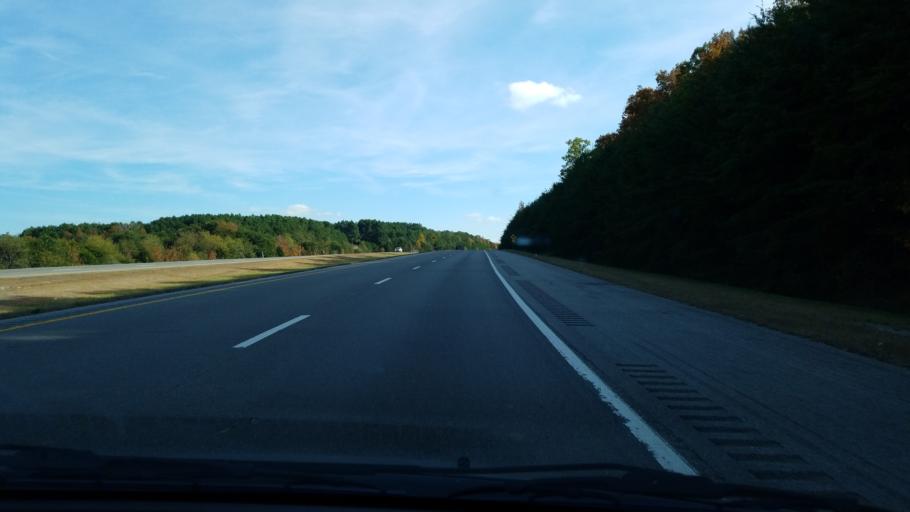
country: US
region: Tennessee
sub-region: Hamilton County
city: Sale Creek
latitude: 35.3429
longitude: -85.1703
